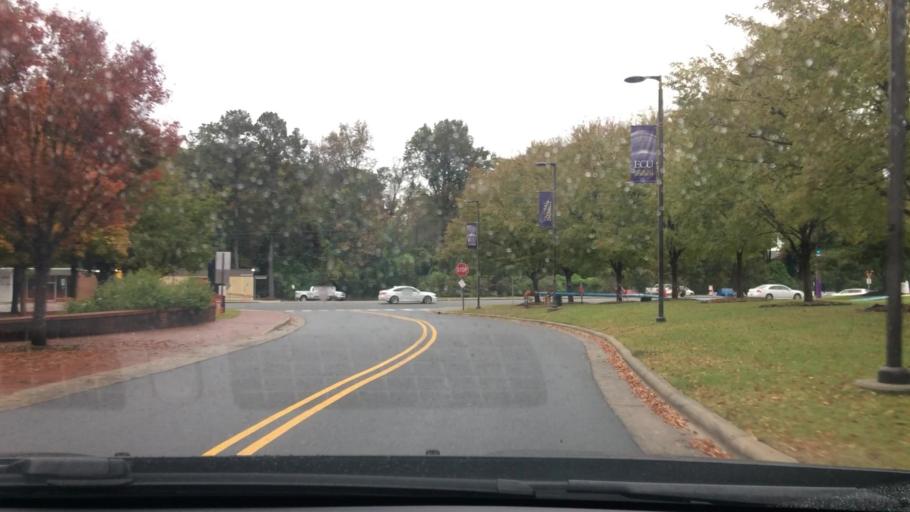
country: US
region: North Carolina
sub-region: Pitt County
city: Greenville
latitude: 35.6052
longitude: -77.3658
